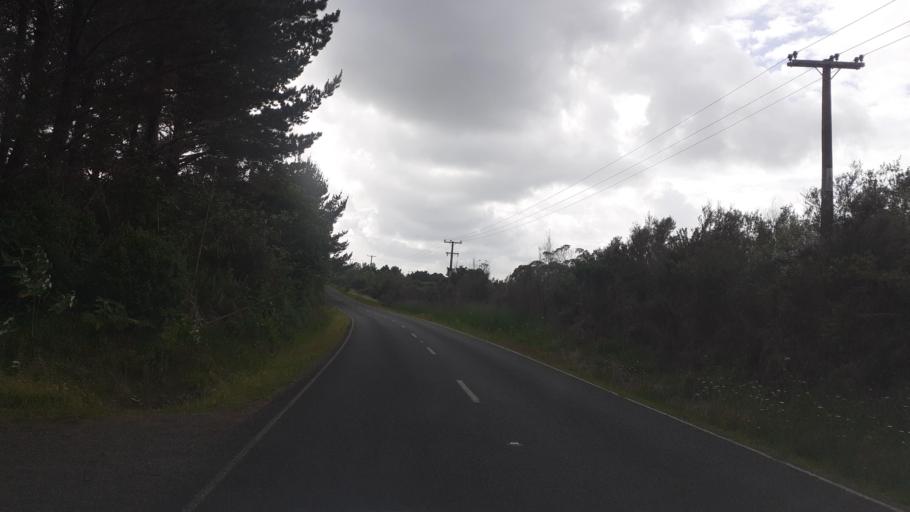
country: NZ
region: Northland
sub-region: Far North District
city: Kerikeri
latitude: -35.2255
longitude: 174.0147
